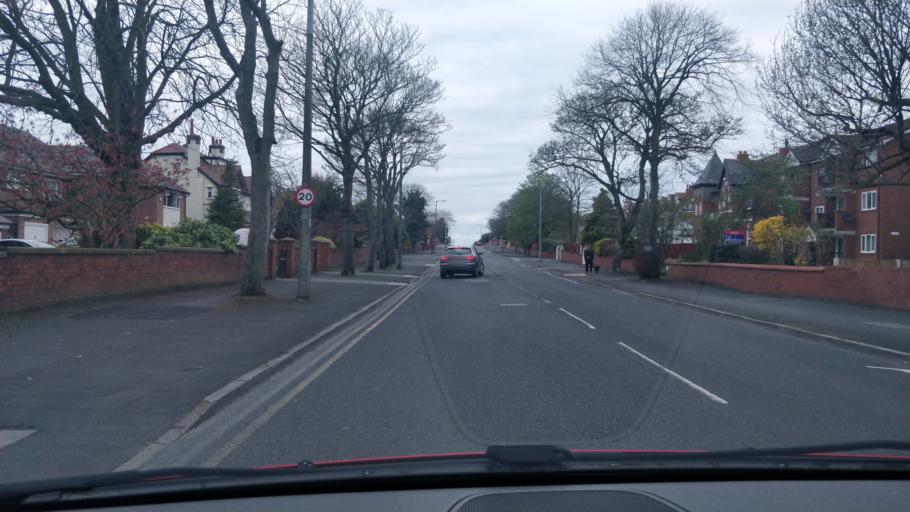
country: GB
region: England
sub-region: Sefton
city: Formby
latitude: 53.6025
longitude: -3.0434
